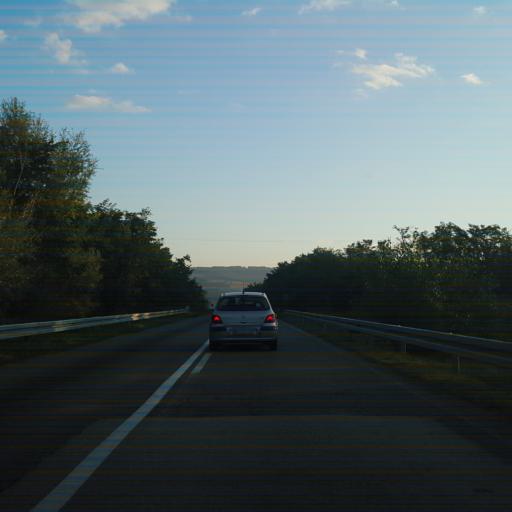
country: RS
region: Central Serbia
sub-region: Zajecarski Okrug
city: Zajecar
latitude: 44.0906
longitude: 22.3435
